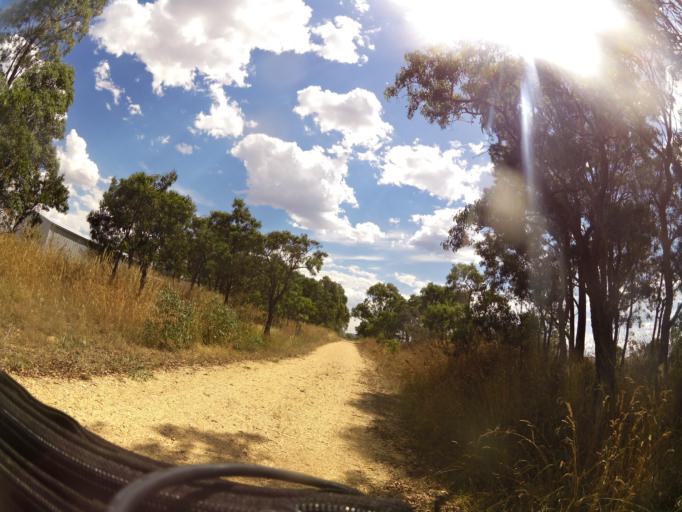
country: AU
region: Victoria
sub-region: Wellington
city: Heyfield
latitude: -37.9765
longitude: 146.7593
